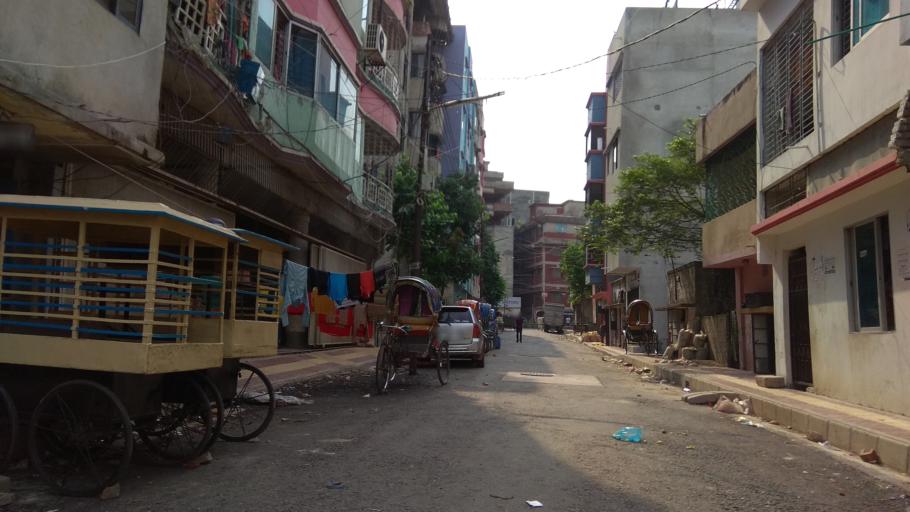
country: BD
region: Dhaka
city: Azimpur
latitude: 23.8119
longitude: 90.3599
